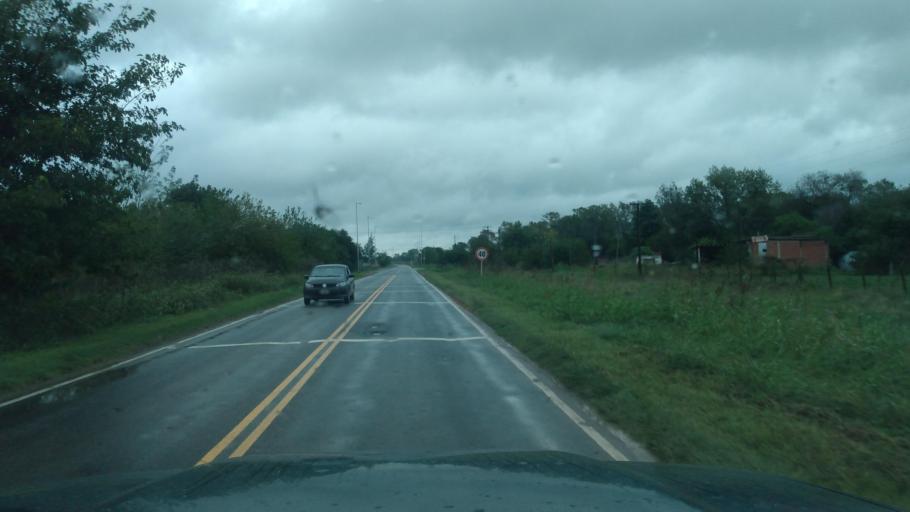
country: AR
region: Buenos Aires
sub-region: Partido de Lujan
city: Lujan
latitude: -34.4849
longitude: -59.0797
